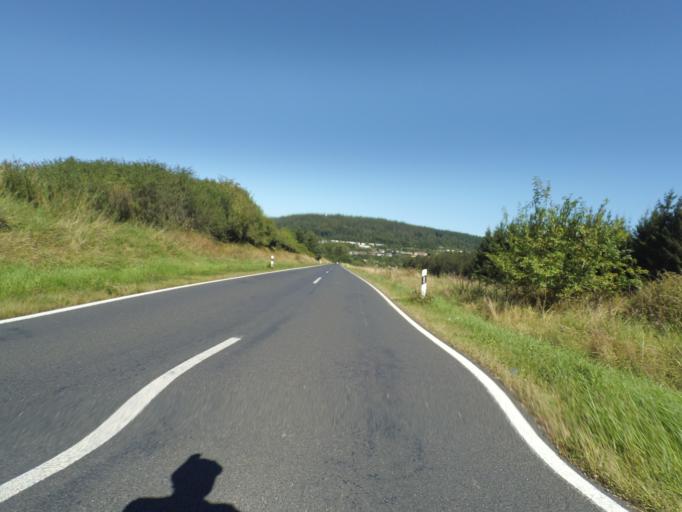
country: DE
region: Rheinland-Pfalz
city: Junkerath
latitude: 50.3424
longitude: 6.5713
